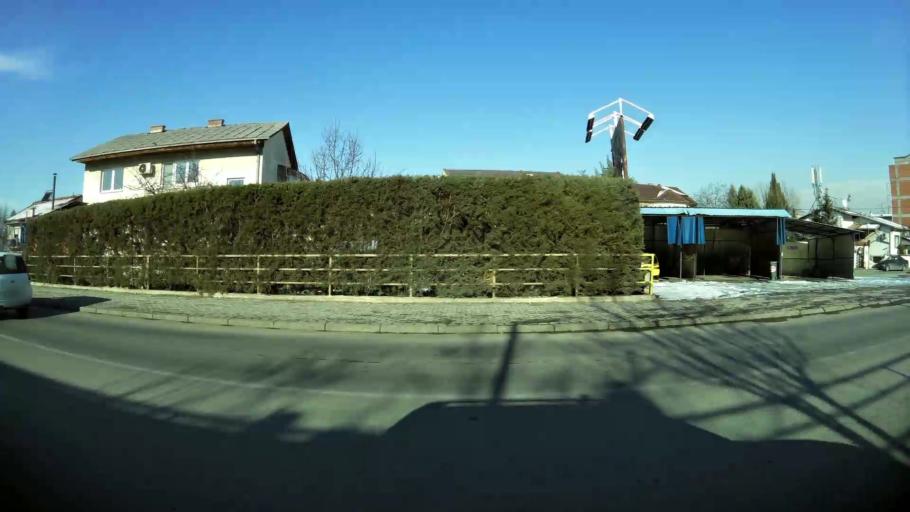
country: MK
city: Krushopek
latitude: 41.9998
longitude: 21.3804
